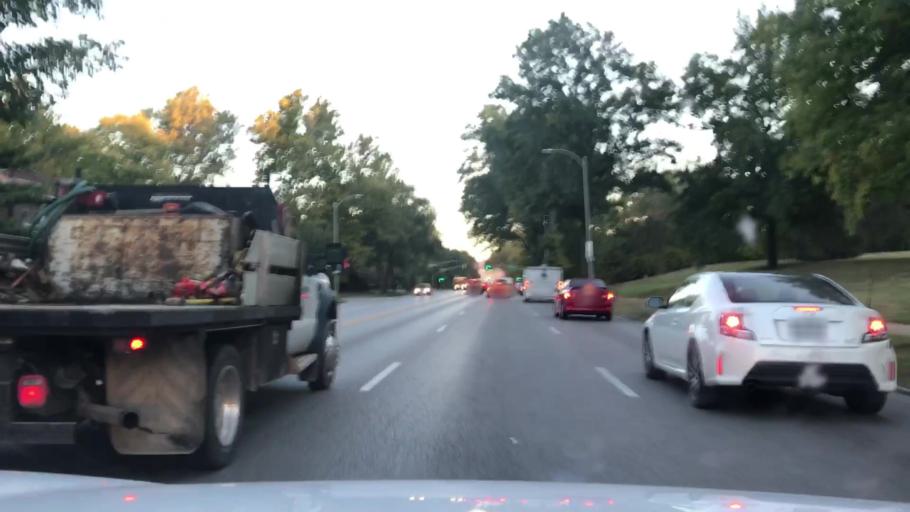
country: US
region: Missouri
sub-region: Saint Louis County
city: Richmond Heights
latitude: 38.6082
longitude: -90.2685
